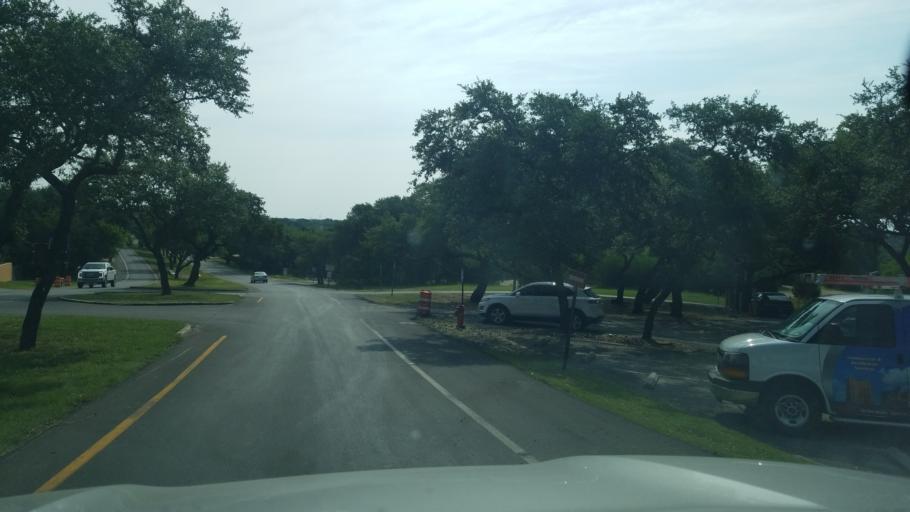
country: US
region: Texas
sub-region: Bexar County
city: Scenic Oaks
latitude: 29.7200
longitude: -98.6647
